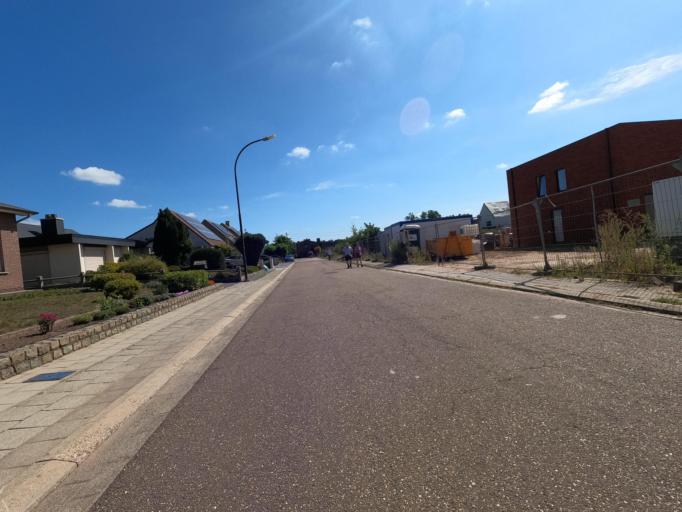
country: BE
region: Flanders
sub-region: Provincie Vlaams-Brabant
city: Scherpenheuvel-Zichem
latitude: 51.0209
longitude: 4.9943
